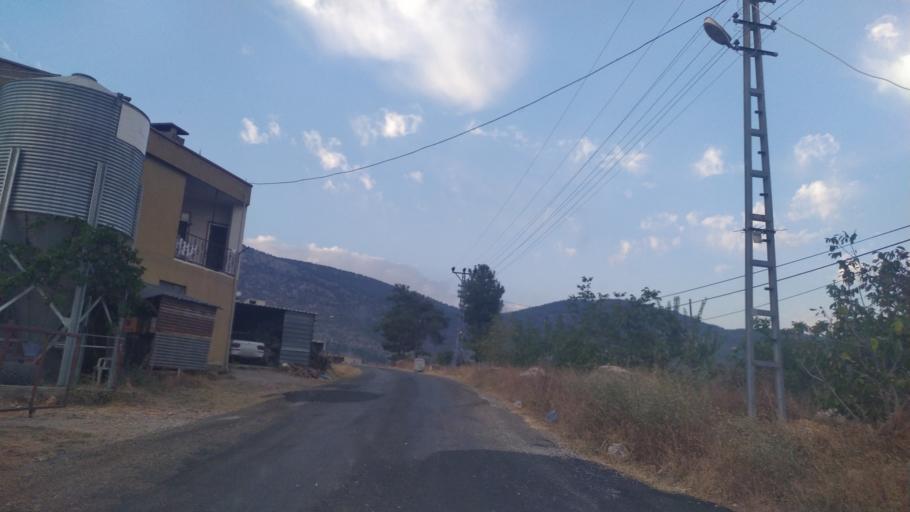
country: TR
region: Mersin
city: Camliyayla
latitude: 37.2338
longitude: 34.7176
